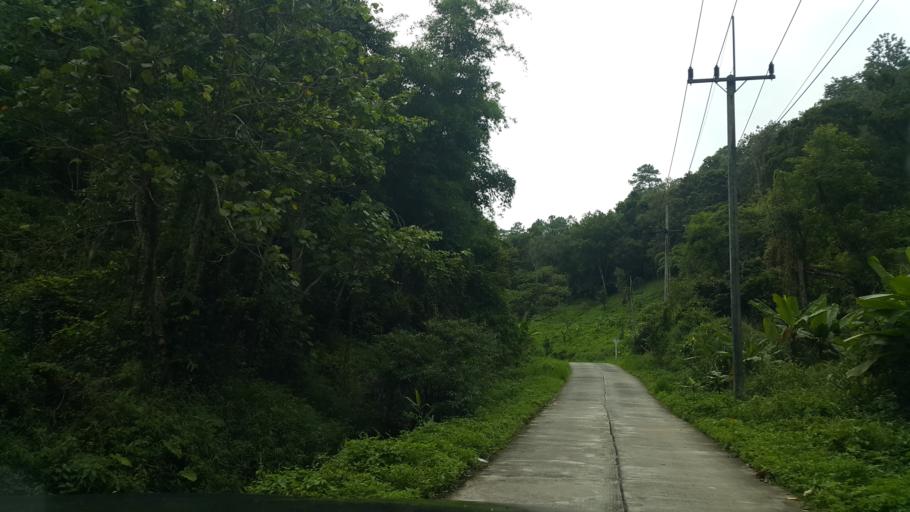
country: TH
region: Lampang
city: Wang Nuea
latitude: 19.0807
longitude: 99.3853
